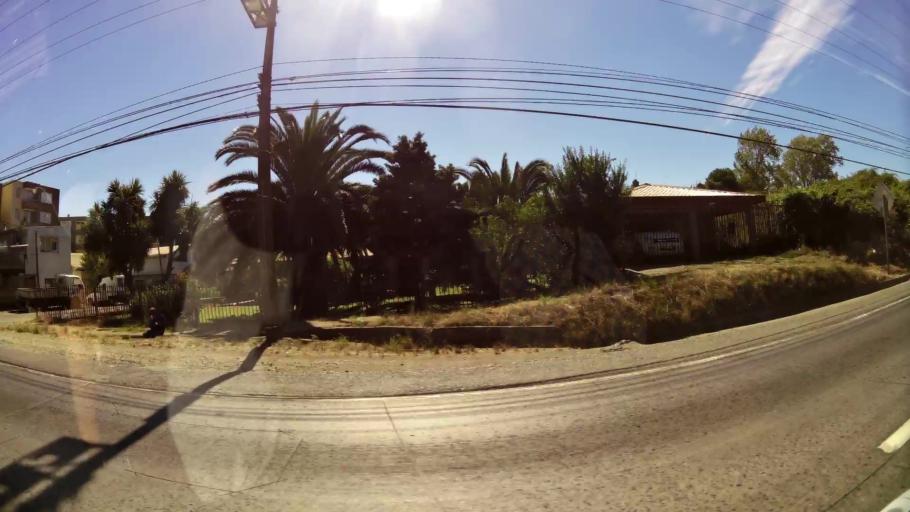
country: CL
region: Biobio
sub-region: Provincia de Concepcion
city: Penco
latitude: -36.7793
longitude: -73.0194
